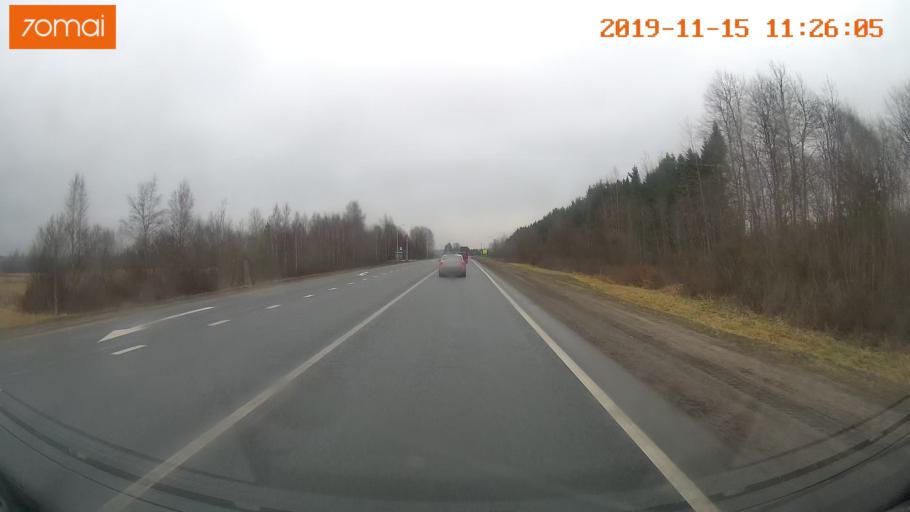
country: RU
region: Vologda
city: Molochnoye
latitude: 59.1653
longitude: 39.4384
